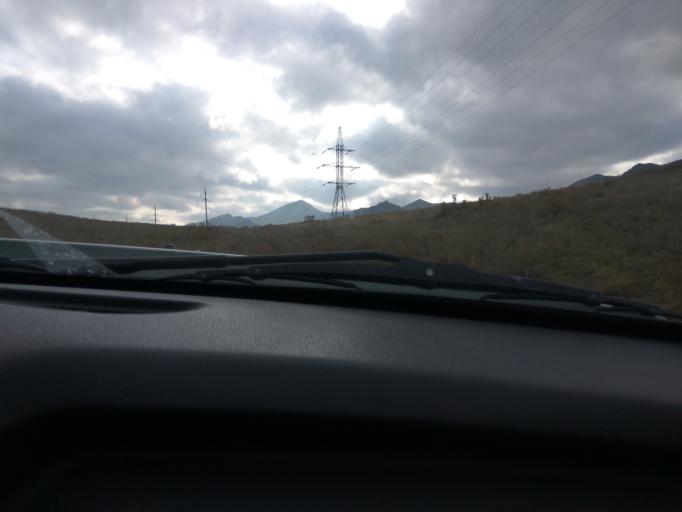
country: RU
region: Dagestan
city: Korkmaskala
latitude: 42.9937
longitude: 47.2331
